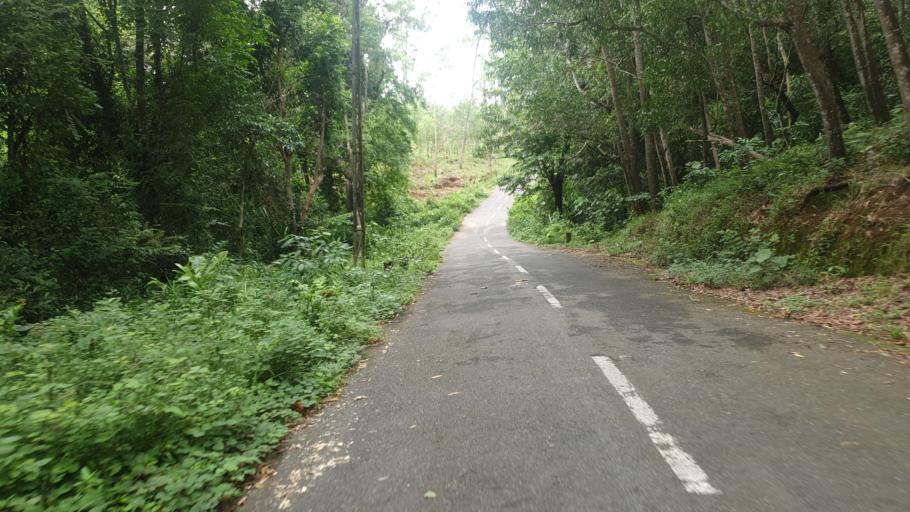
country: IN
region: Kerala
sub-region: Thiruvananthapuram
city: Nedumangad
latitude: 8.6453
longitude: 77.1096
